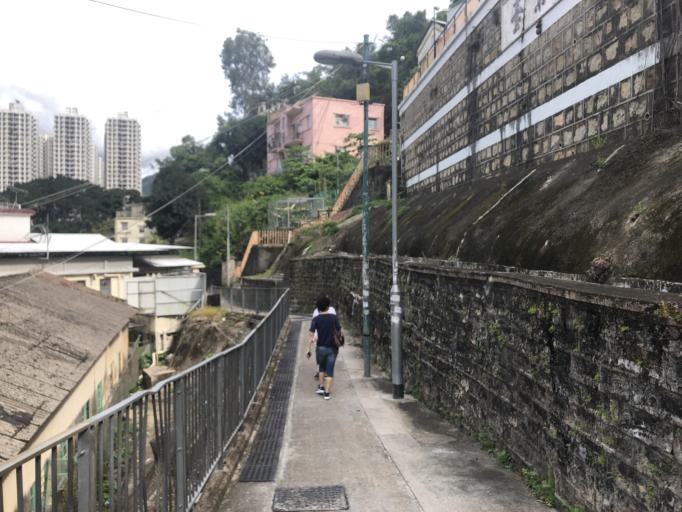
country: HK
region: Sha Tin
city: Sha Tin
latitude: 22.3852
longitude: 114.1860
